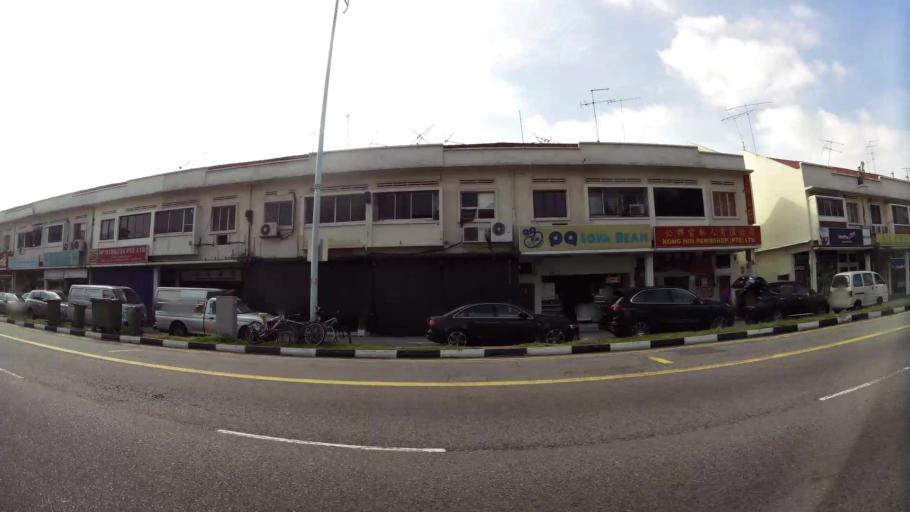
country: SG
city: Singapore
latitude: 1.3180
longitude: 103.9073
